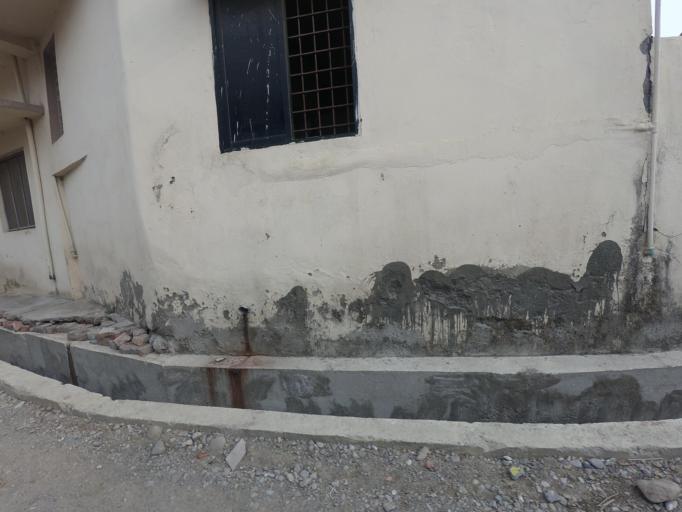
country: NP
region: Western Region
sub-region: Lumbini Zone
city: Bhairahawa
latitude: 27.5055
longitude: 83.4490
